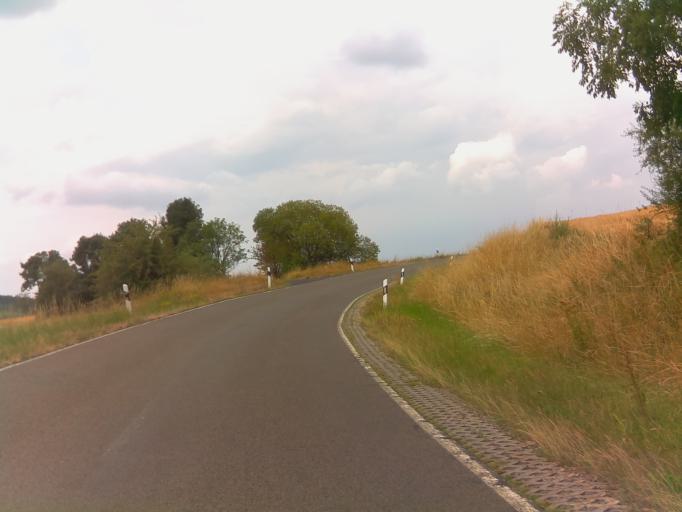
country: DE
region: Hesse
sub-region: Regierungsbezirk Giessen
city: Grebenhain
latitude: 50.4520
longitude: 9.2727
